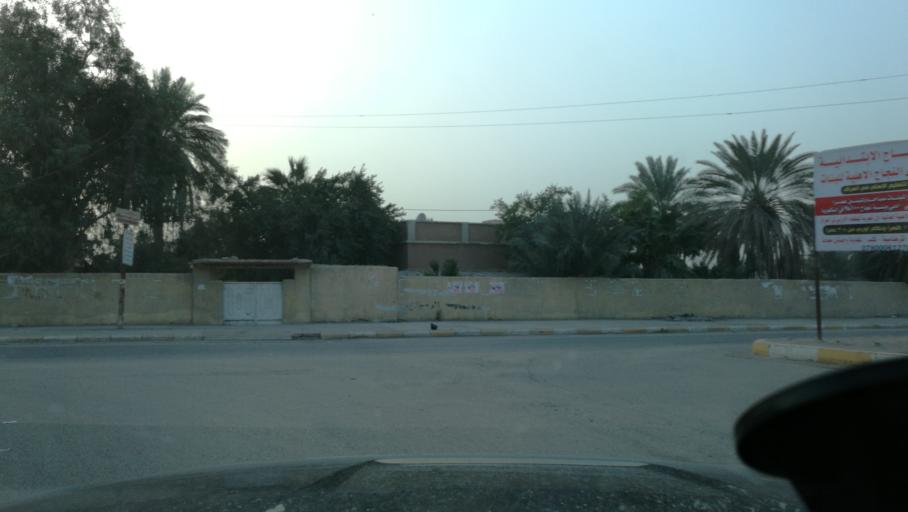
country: IQ
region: Dhi Qar
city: An Nasiriyah
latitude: 31.0398
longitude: 46.2408
